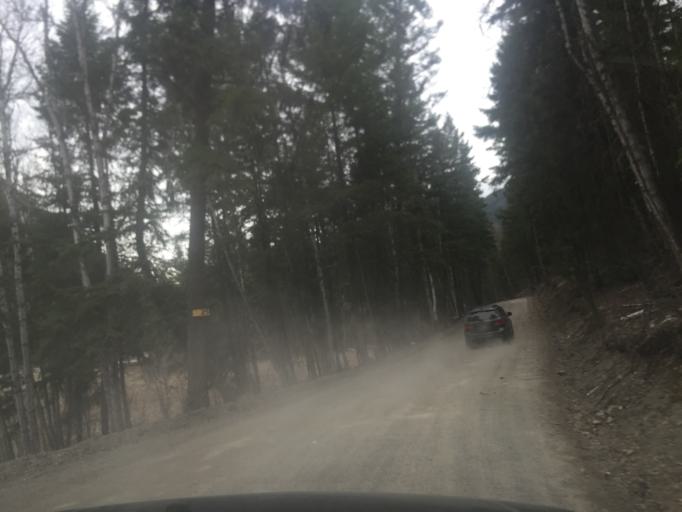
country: CA
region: British Columbia
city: Chase
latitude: 51.3968
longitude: -120.1253
